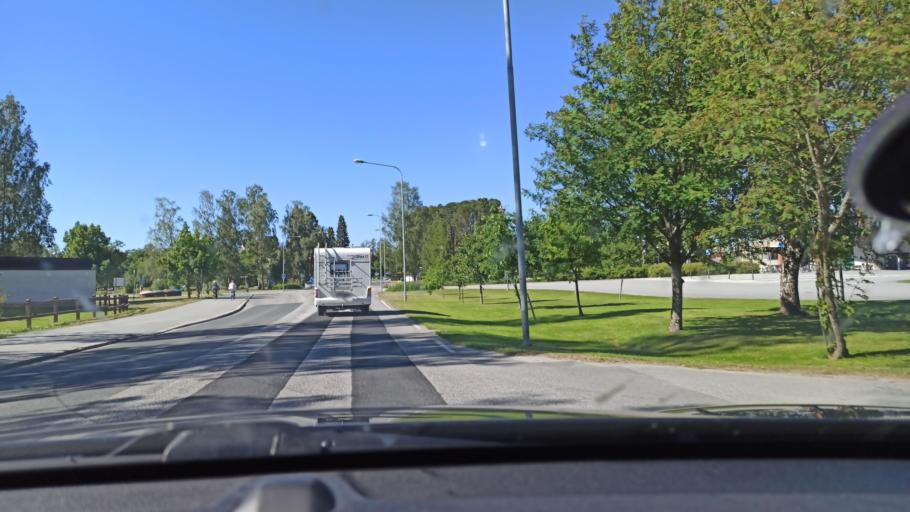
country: FI
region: Ostrobothnia
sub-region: Jakobstadsregionen
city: Jakobstad
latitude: 63.6734
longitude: 22.7138
